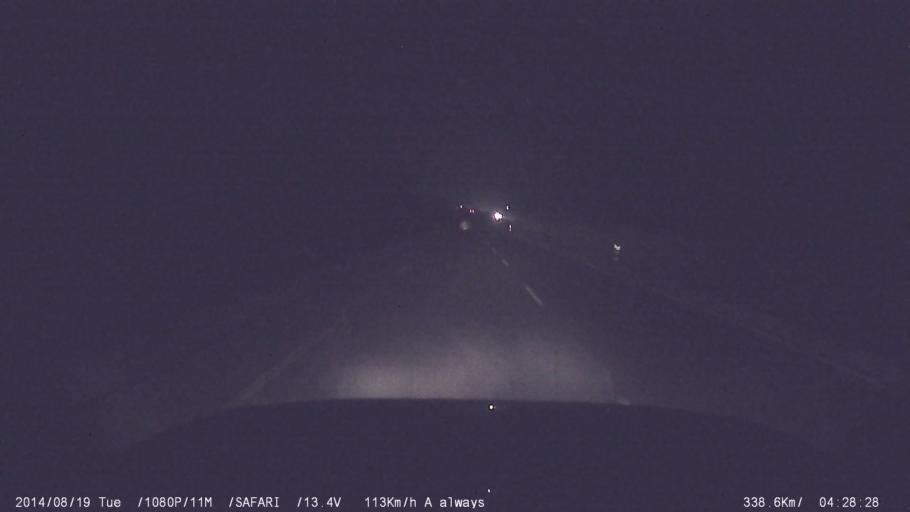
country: IN
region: Tamil Nadu
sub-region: Erode
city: Vijayapuri
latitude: 11.2473
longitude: 77.5249
